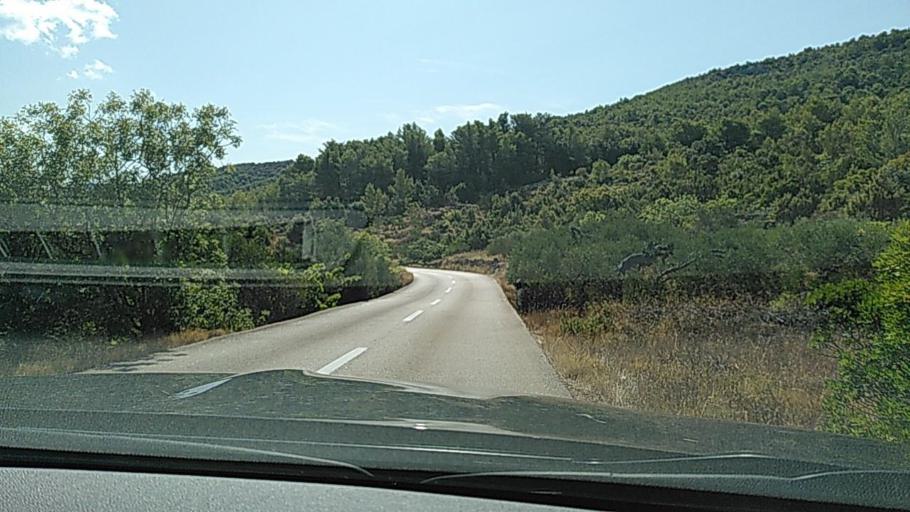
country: HR
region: Splitsko-Dalmatinska
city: Jelsa
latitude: 43.1449
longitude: 16.8026
